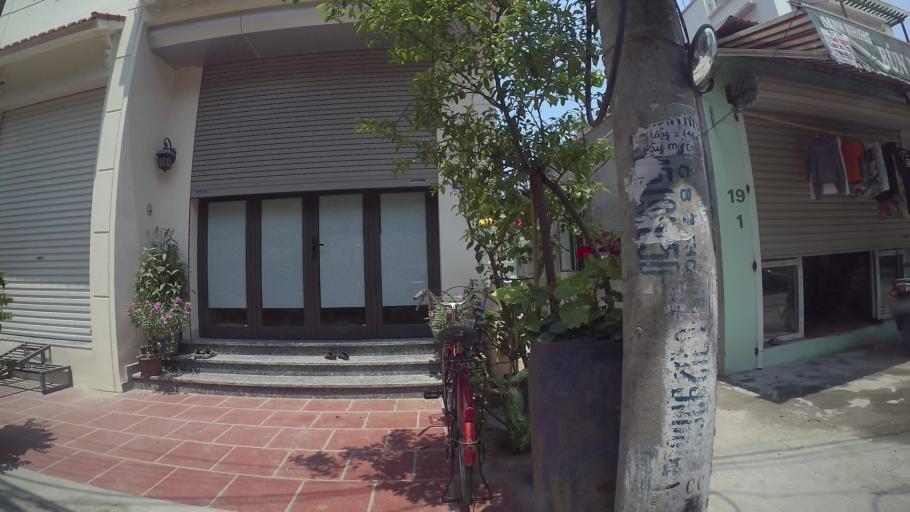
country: VN
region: Ha Noi
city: Trau Quy
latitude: 21.0302
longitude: 105.9103
